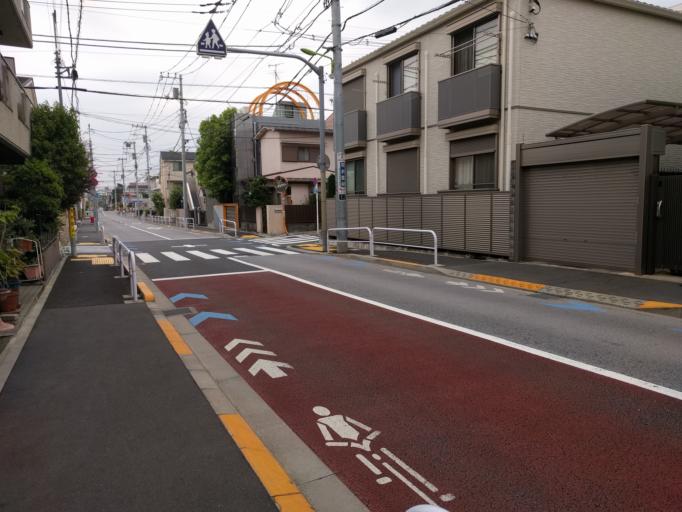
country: JP
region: Tokyo
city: Tokyo
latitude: 35.6045
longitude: 139.6573
